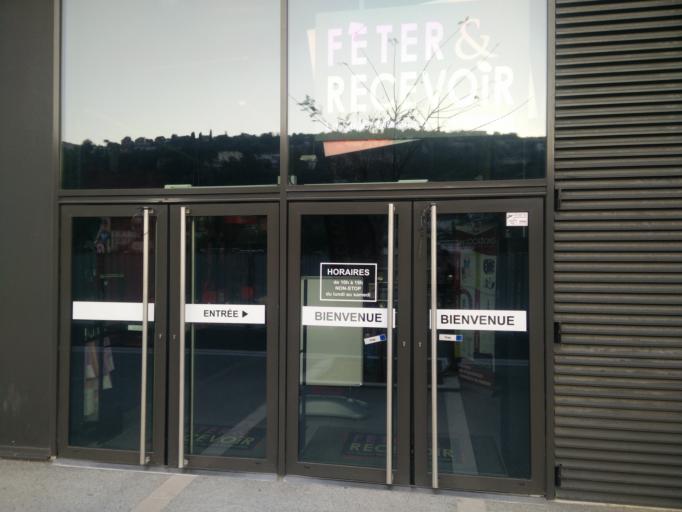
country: FR
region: Provence-Alpes-Cote d'Azur
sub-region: Departement des Alpes-Maritimes
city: Saint-Laurent-du-Var
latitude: 43.7070
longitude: 7.1938
